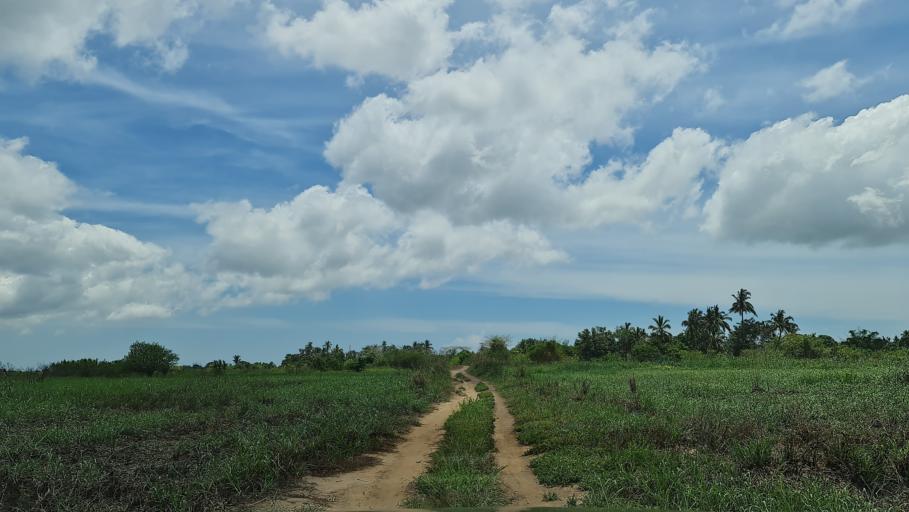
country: MZ
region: Zambezia
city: Quelimane
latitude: -17.5828
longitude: 37.3781
